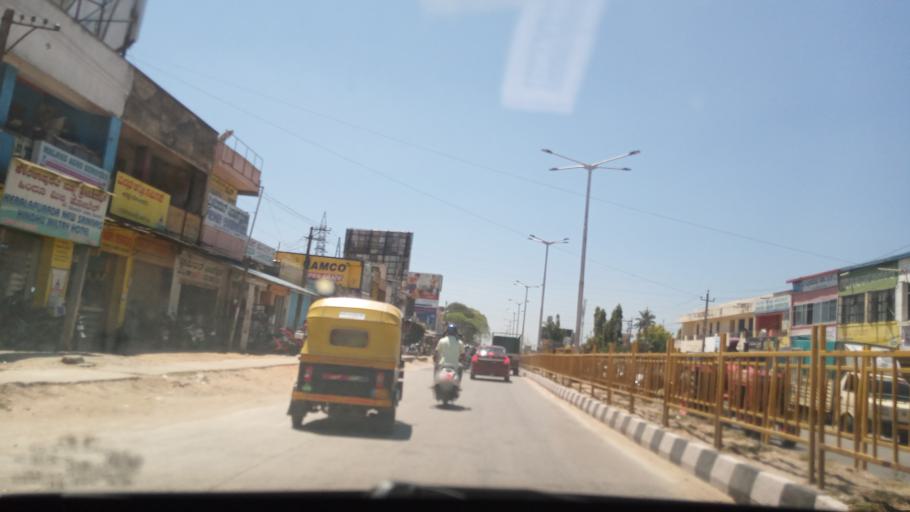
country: IN
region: Karnataka
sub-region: Hassan
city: Hassan
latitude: 12.9996
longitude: 76.0931
